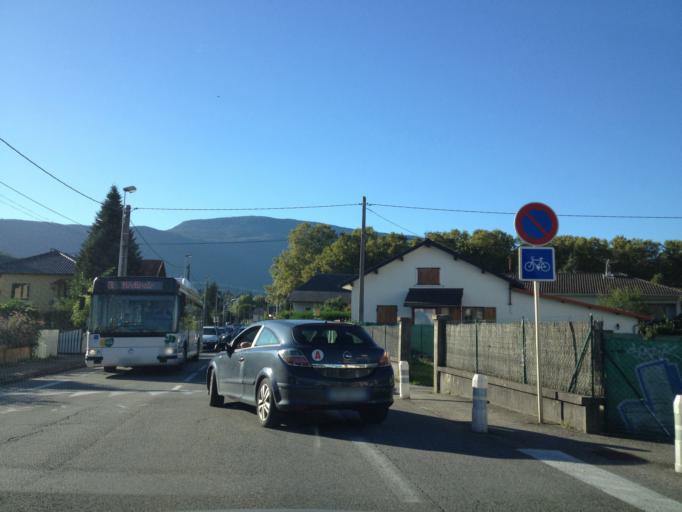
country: FR
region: Rhone-Alpes
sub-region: Departement de la Savoie
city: Cognin
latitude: 45.5804
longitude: 5.8915
